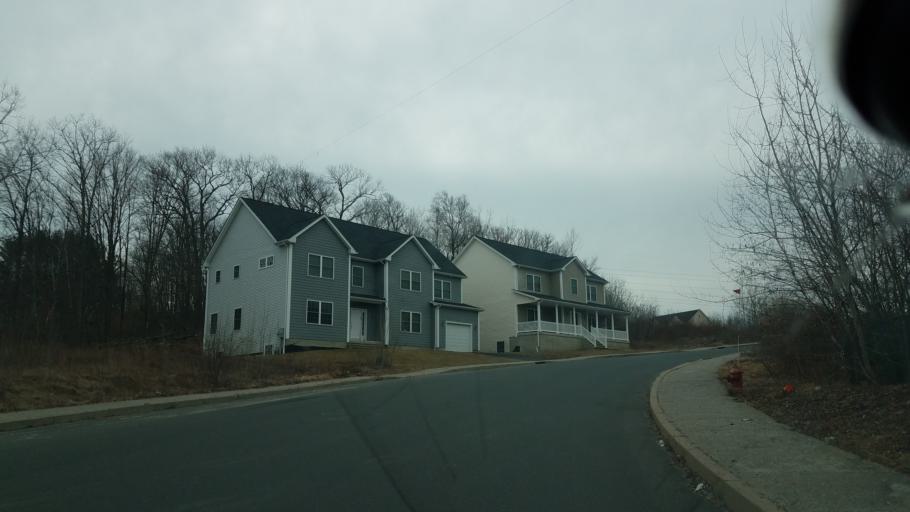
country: US
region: Connecticut
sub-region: New Haven County
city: Waterbury
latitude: 41.5944
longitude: -73.0323
